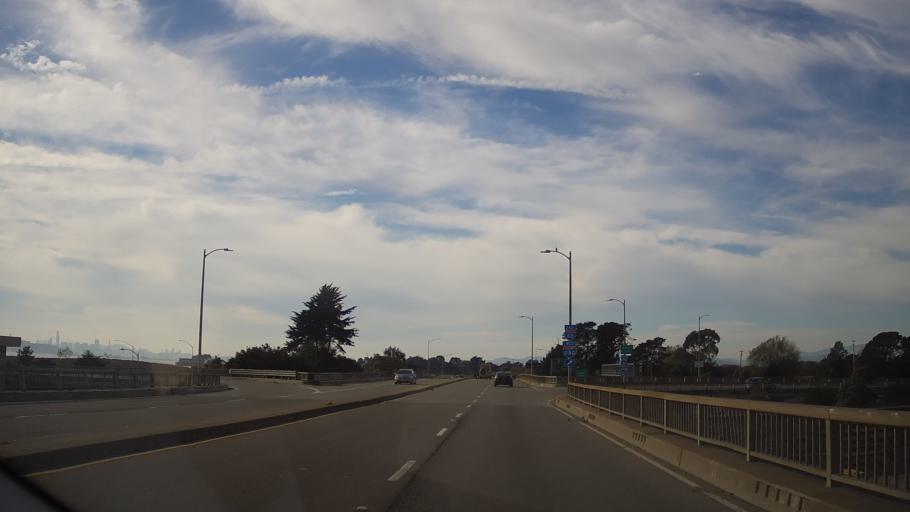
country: US
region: California
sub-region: Alameda County
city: Albany
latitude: 37.8671
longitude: -122.3022
